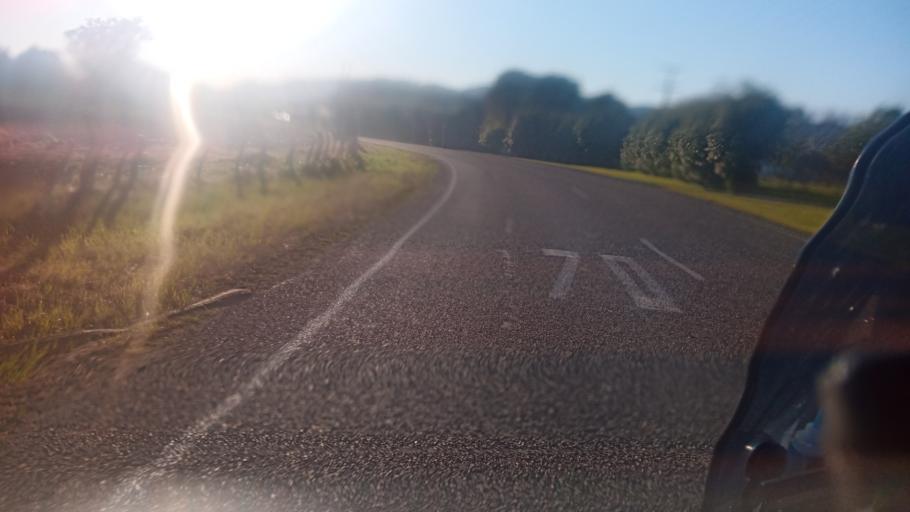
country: NZ
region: Hawke's Bay
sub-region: Wairoa District
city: Wairoa
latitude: -39.0448
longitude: 177.7534
